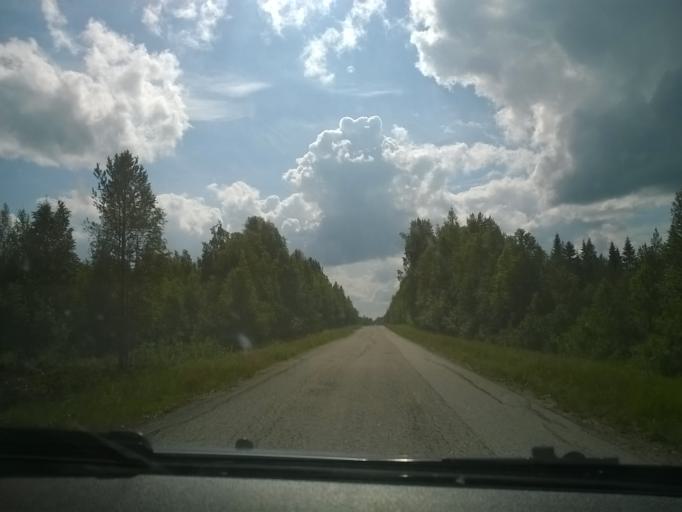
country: FI
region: Kainuu
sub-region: Kehys-Kainuu
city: Kuhmo
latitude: 64.4107
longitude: 29.7690
